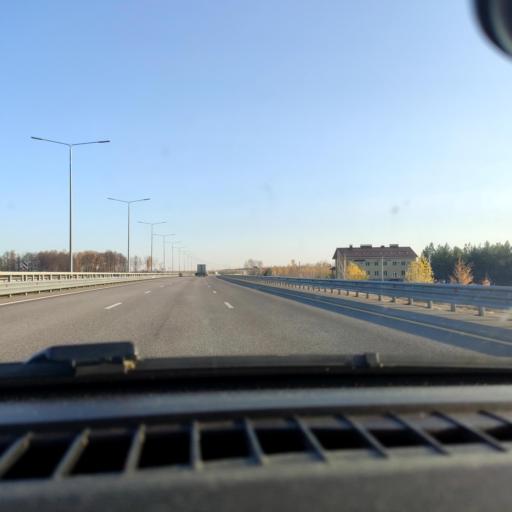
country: RU
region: Voronezj
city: Somovo
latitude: 51.7820
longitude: 39.2928
